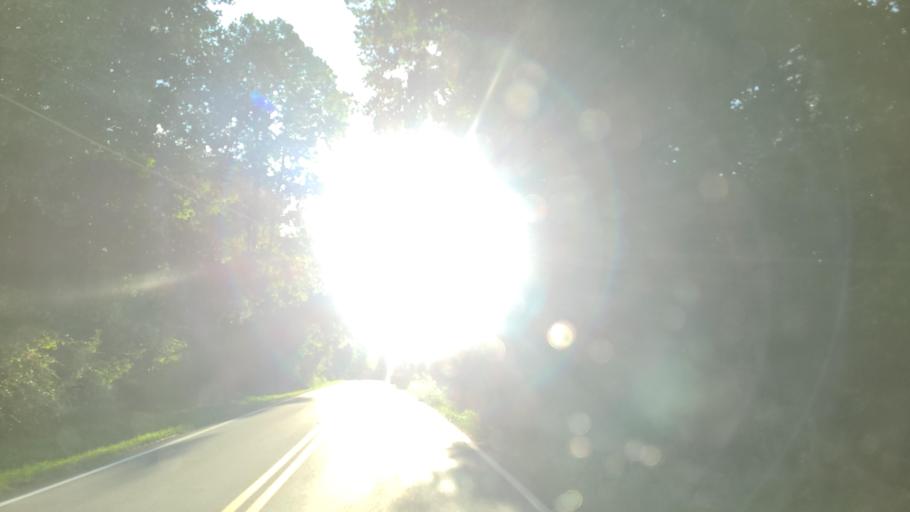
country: US
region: Georgia
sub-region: Fulton County
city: Milton
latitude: 34.1724
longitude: -84.3573
